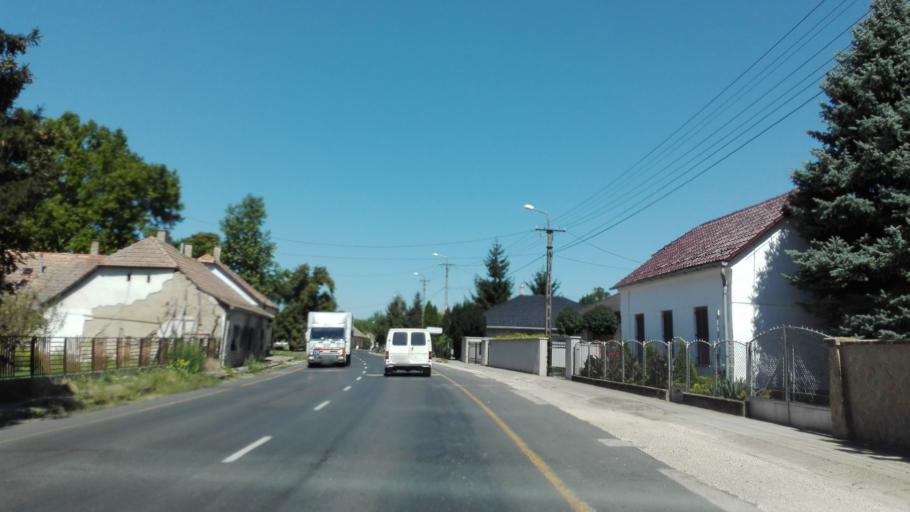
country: HU
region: Fejer
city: Mezoszilas
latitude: 46.8109
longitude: 18.4833
